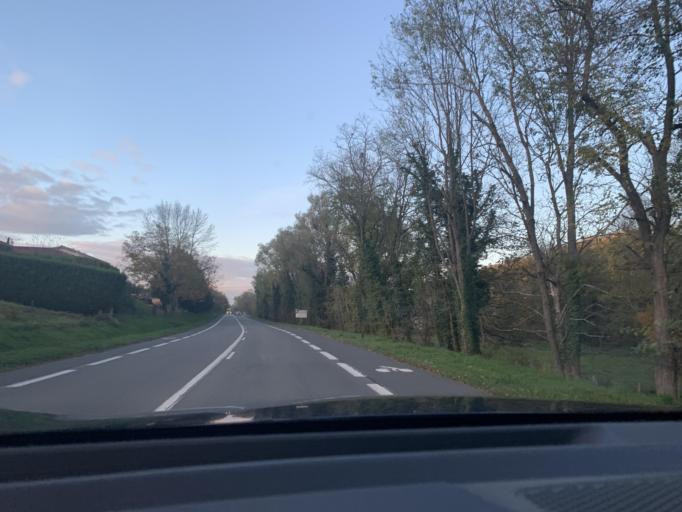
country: FR
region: Rhone-Alpes
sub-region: Departement du Rhone
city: Liergues
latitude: 45.9573
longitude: 4.6673
